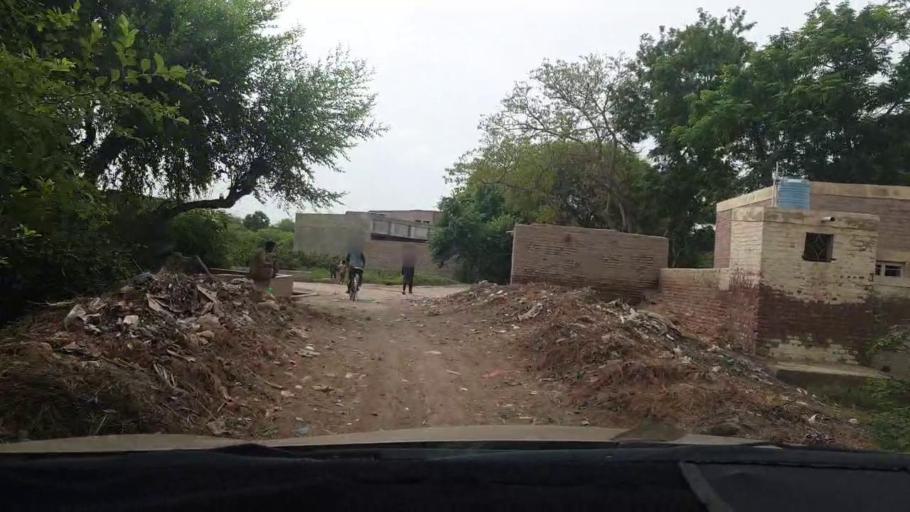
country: PK
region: Sindh
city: Naudero
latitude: 27.6302
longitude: 68.3101
